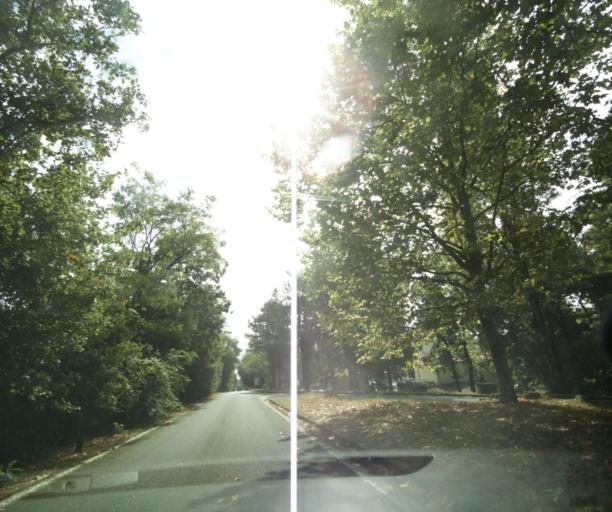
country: FR
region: Poitou-Charentes
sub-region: Departement de la Charente-Maritime
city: Pons
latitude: 45.6104
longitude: -0.6001
